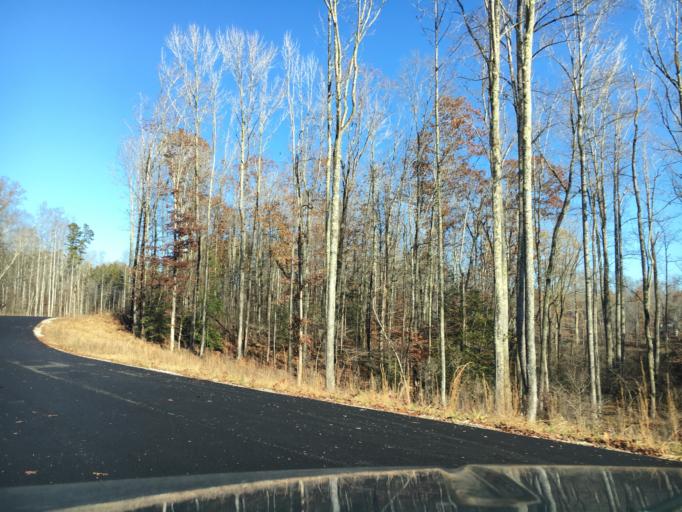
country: US
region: Virginia
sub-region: Goochland County
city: Goochland
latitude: 37.6937
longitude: -77.8418
